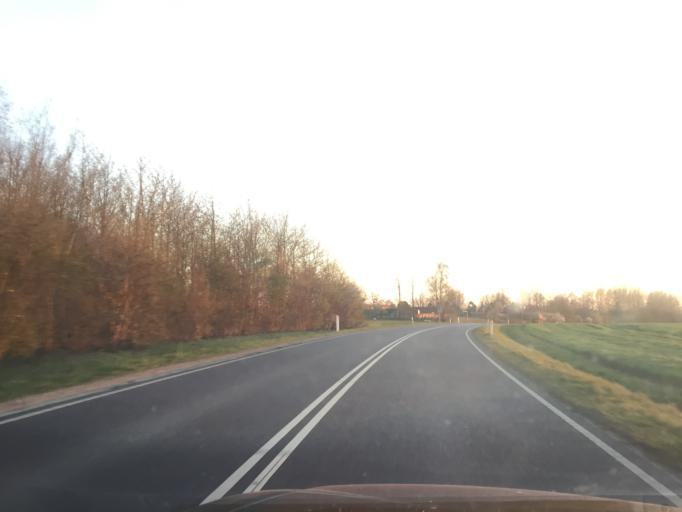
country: DK
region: Capital Region
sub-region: Allerod Kommune
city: Lynge
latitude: 55.8500
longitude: 12.2836
